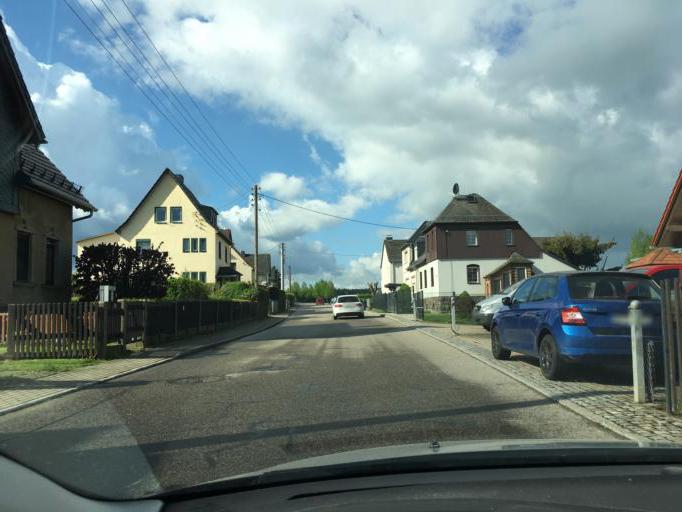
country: DE
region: Saxony
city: Hohenstein-Ernstthal
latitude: 50.8311
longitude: 12.7068
